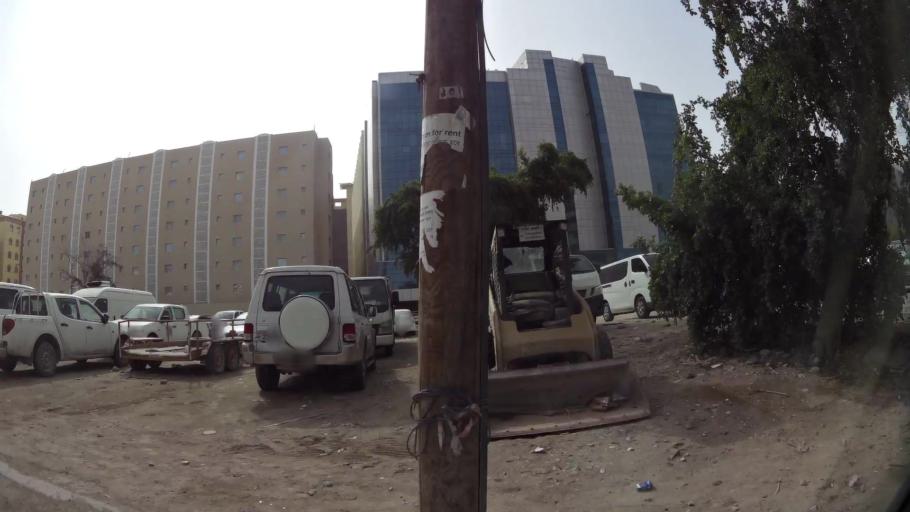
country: QA
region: Baladiyat ad Dawhah
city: Doha
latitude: 25.2746
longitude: 51.5429
